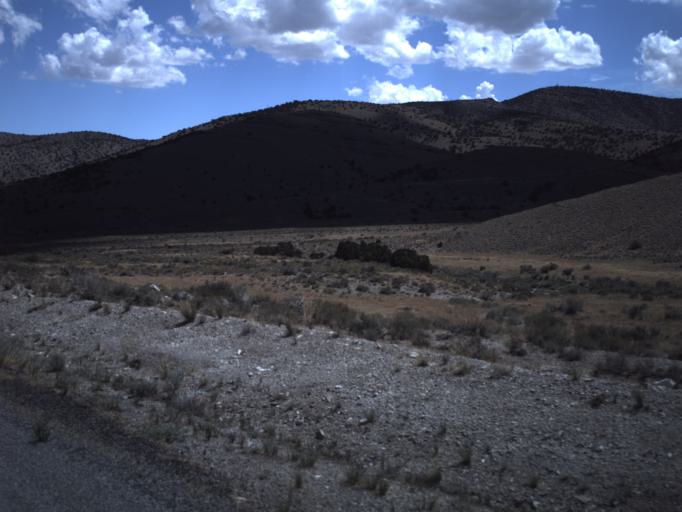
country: US
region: Utah
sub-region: Beaver County
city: Milford
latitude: 39.0779
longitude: -113.6170
